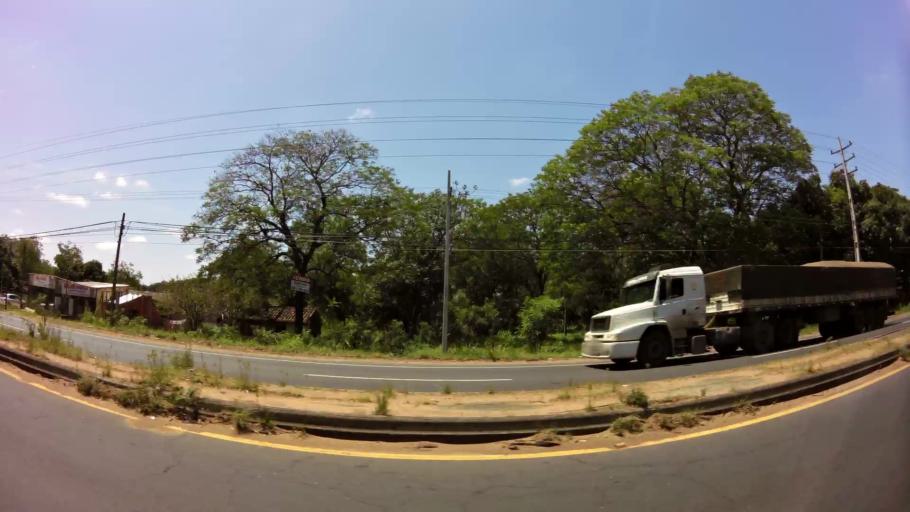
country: PY
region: Central
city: San Antonio
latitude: -25.4088
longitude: -57.5416
